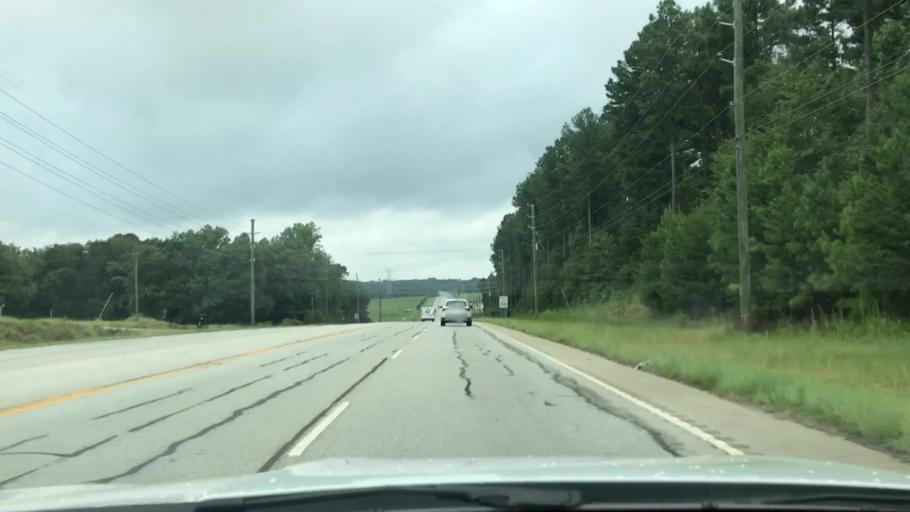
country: US
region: South Carolina
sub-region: Spartanburg County
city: Roebuck
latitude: 34.8606
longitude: -82.0221
